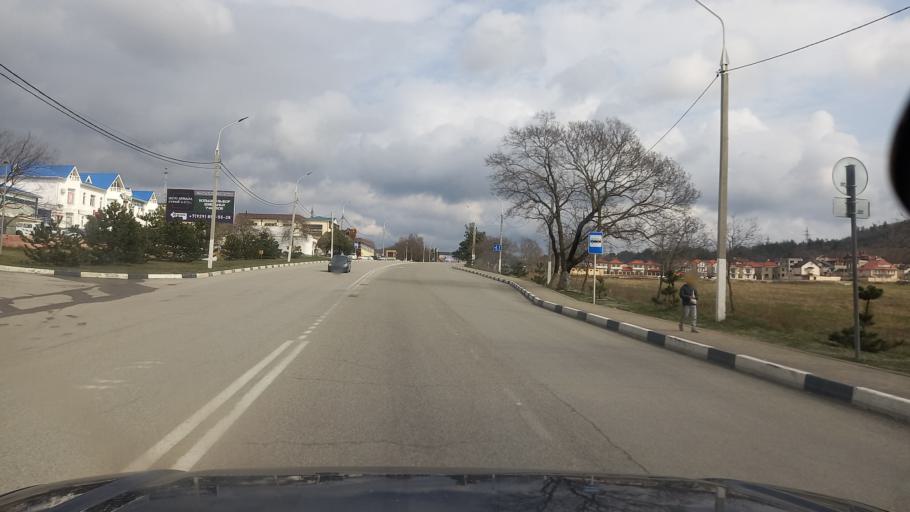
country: RU
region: Krasnodarskiy
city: Gelendzhik
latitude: 44.5544
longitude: 38.1129
